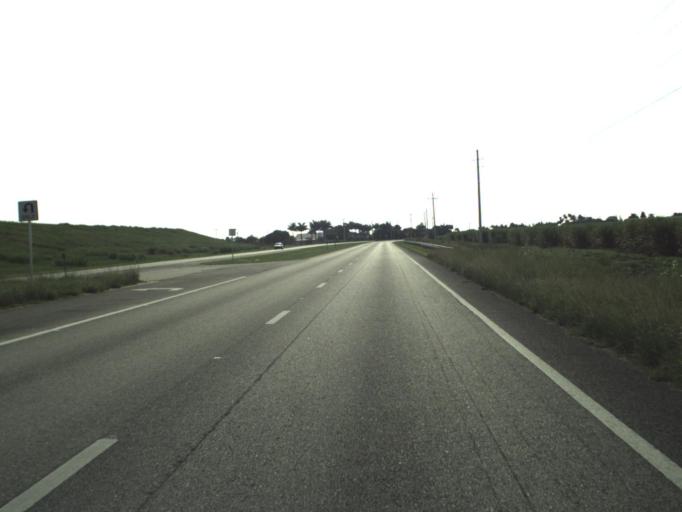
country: US
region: Florida
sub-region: Palm Beach County
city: South Bay
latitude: 26.6803
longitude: -80.7374
